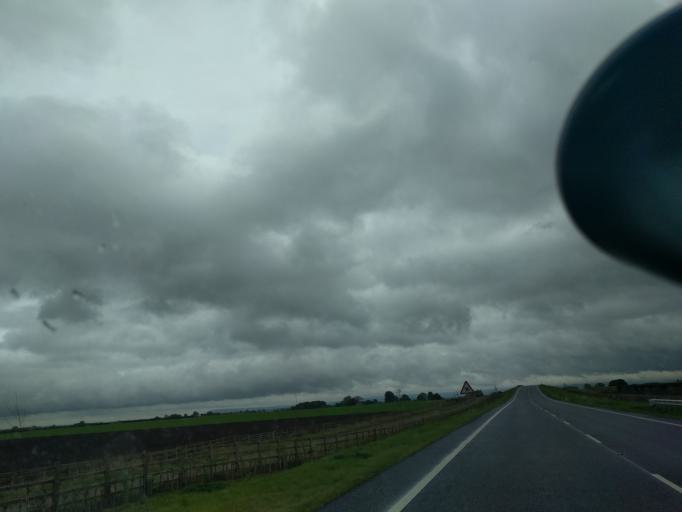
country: GB
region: England
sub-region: North Yorkshire
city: Bedale
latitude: 54.3128
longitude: -1.5559
